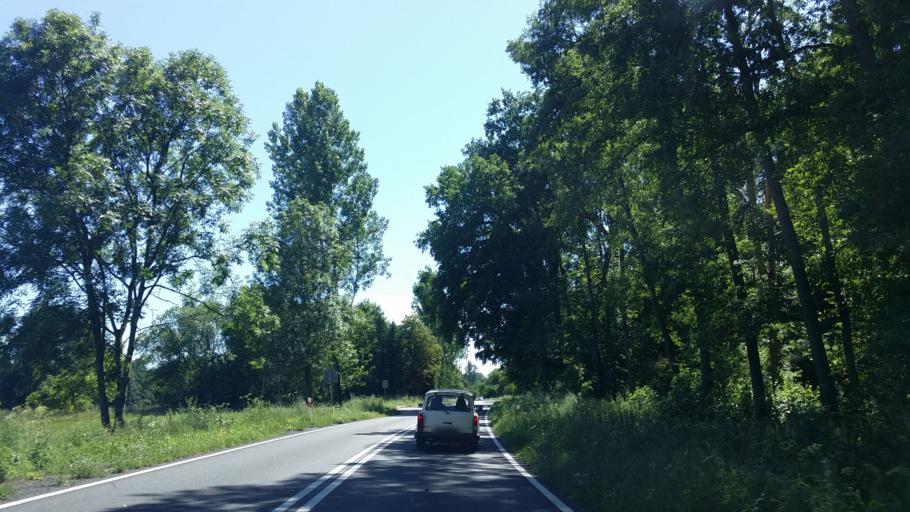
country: PL
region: West Pomeranian Voivodeship
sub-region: Powiat stargardzki
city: Insko
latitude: 53.4739
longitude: 15.5781
